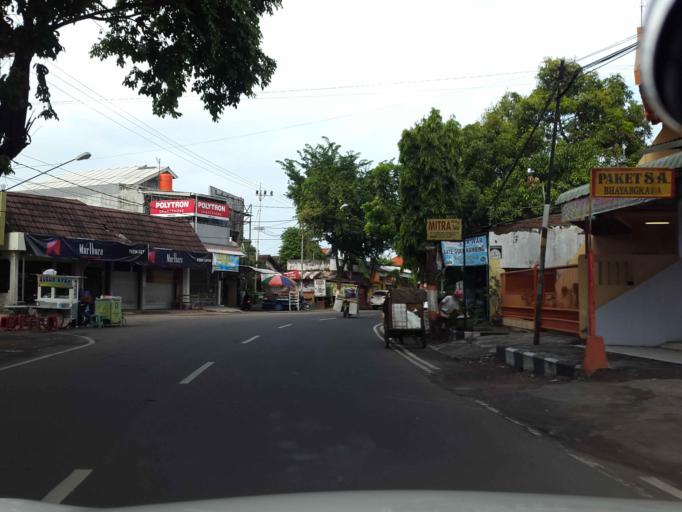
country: ID
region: East Java
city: Soko
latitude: -7.4807
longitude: 112.4317
